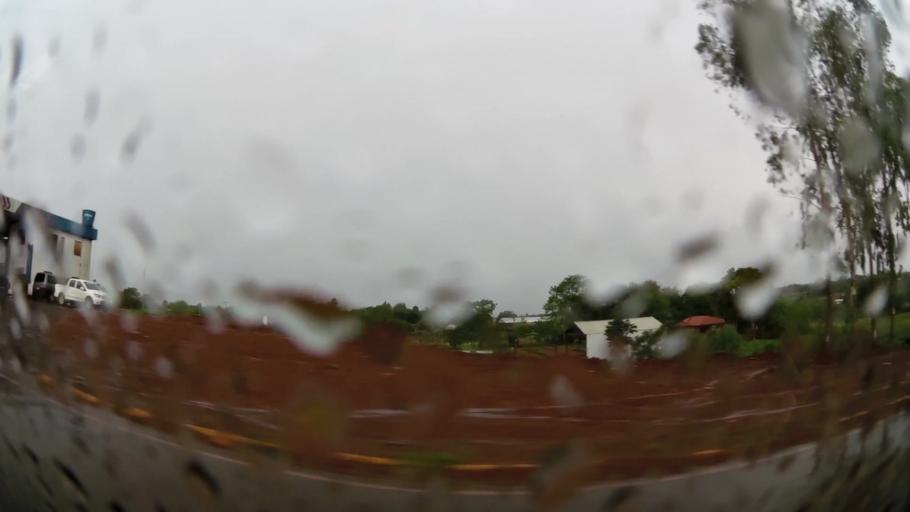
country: PY
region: Alto Parana
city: Presidente Franco
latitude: -25.5286
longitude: -54.6789
